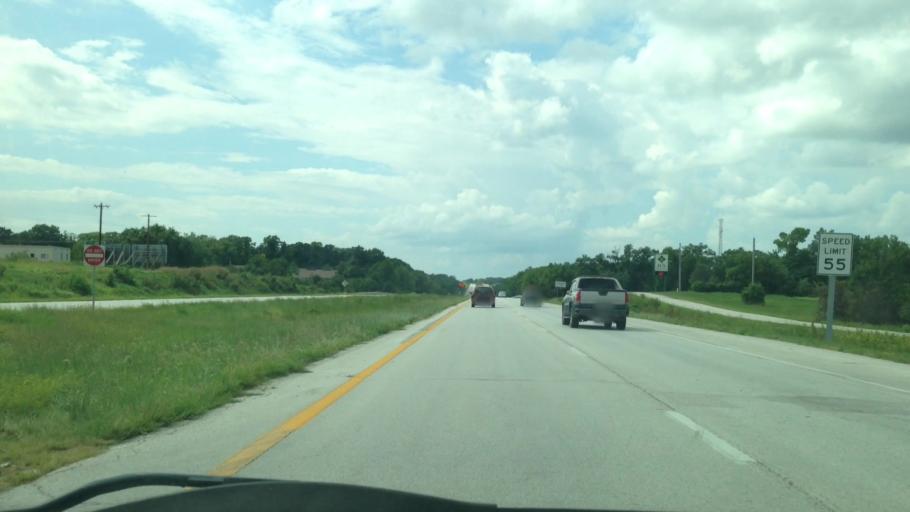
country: US
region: Missouri
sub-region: Marion County
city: Hannibal
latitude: 39.7314
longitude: -91.4003
